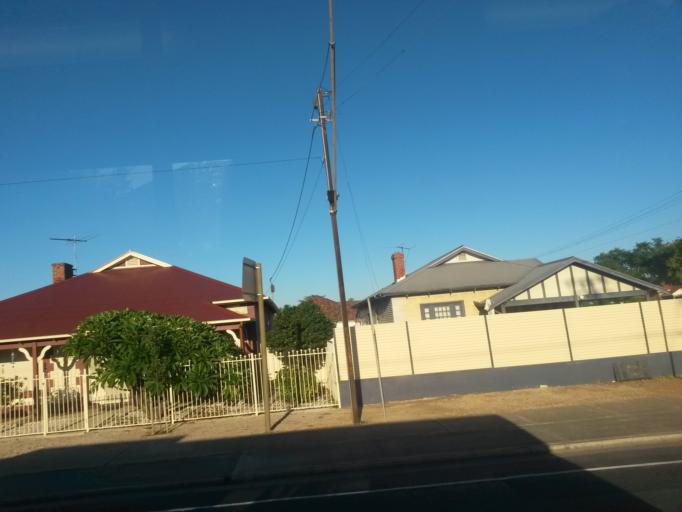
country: AU
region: South Australia
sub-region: Port Adelaide Enfield
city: Alberton
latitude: -34.8526
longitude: 138.5290
